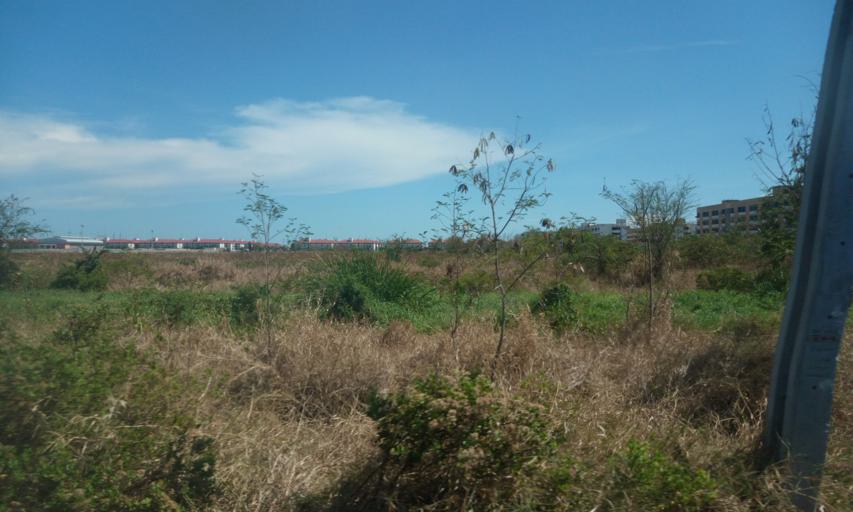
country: TH
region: Samut Prakan
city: Bang Bo District
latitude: 13.5625
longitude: 100.7690
